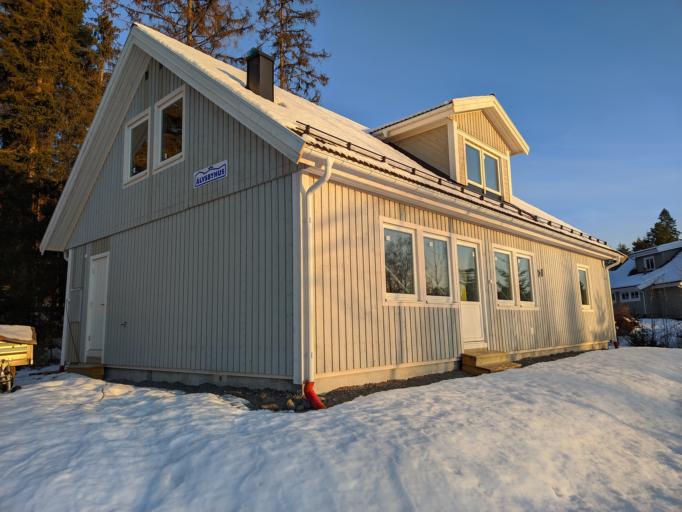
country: NO
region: Hedmark
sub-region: Loten
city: Loten
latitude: 60.7890
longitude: 11.3072
